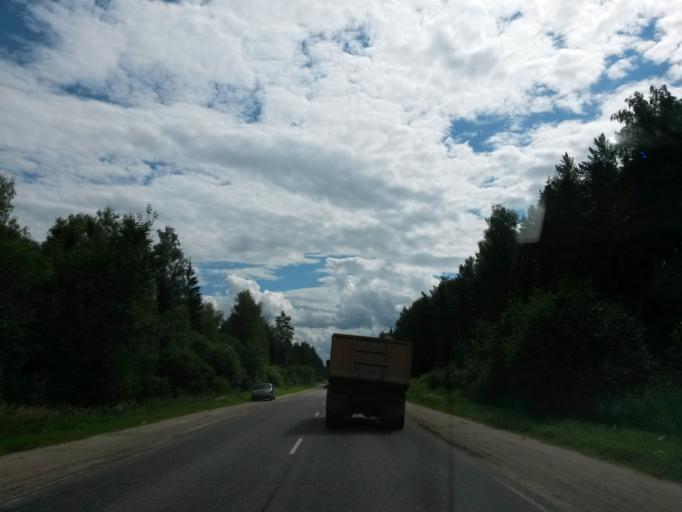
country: RU
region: Ivanovo
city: Novo-Talitsy
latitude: 57.0505
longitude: 40.7360
